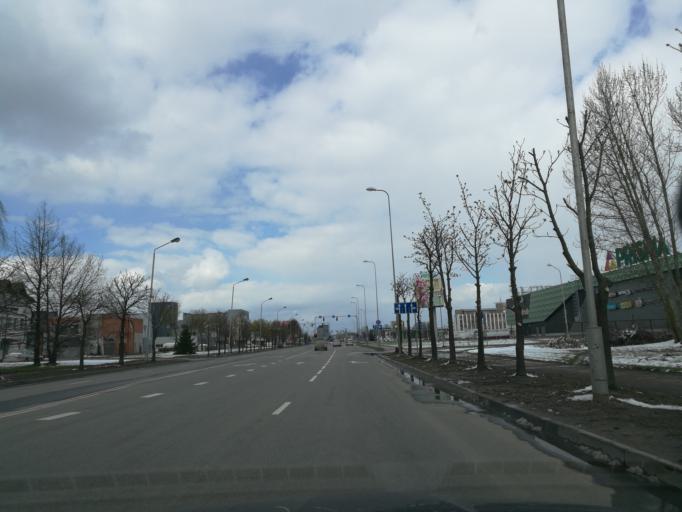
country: LT
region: Kauno apskritis
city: Dainava (Kaunas)
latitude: 54.9076
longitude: 23.9814
